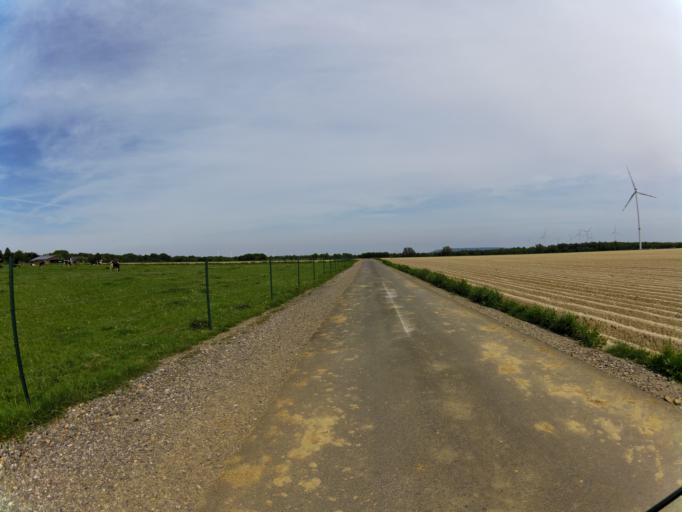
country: DE
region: North Rhine-Westphalia
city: Niedermerz
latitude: 50.8730
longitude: 6.2427
